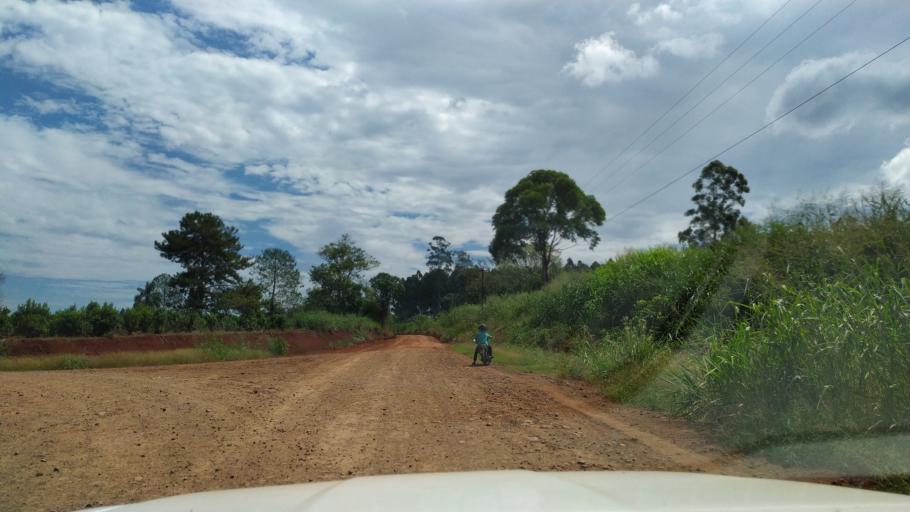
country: AR
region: Misiones
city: Puerto Piray
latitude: -26.5340
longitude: -54.6684
